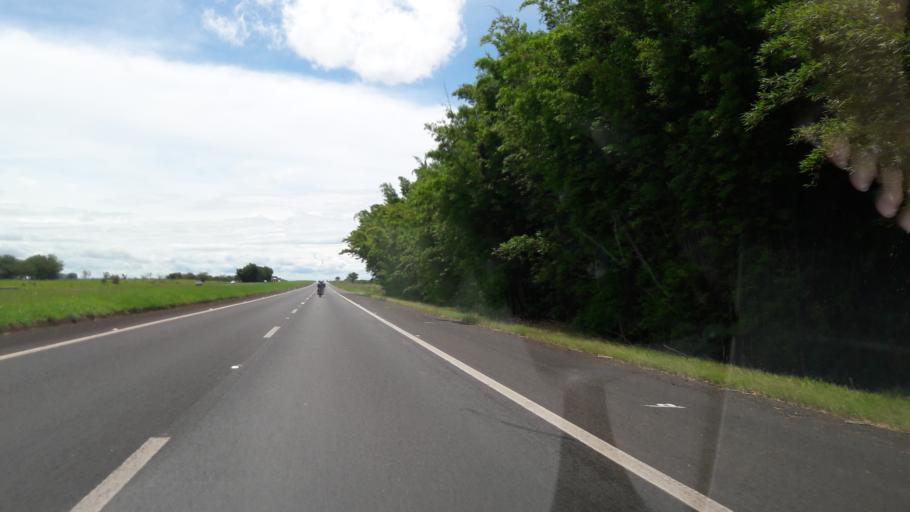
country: BR
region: Sao Paulo
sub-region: Avare
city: Avare
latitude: -22.9494
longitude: -48.8833
